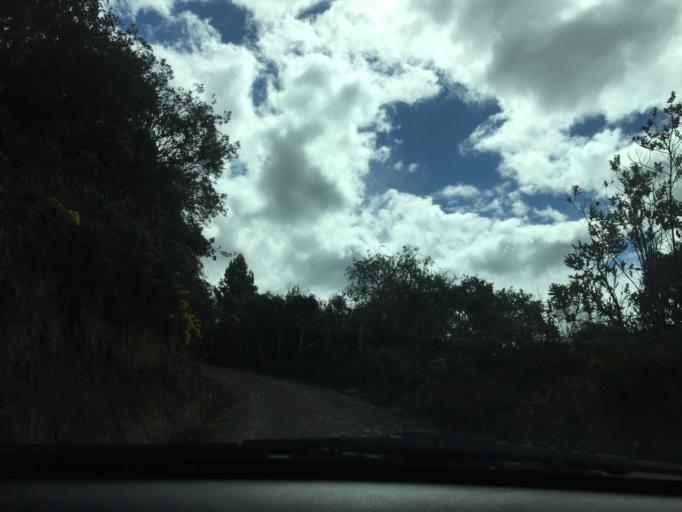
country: CO
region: Cundinamarca
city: Gachancipa
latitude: 4.9597
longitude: -73.8807
